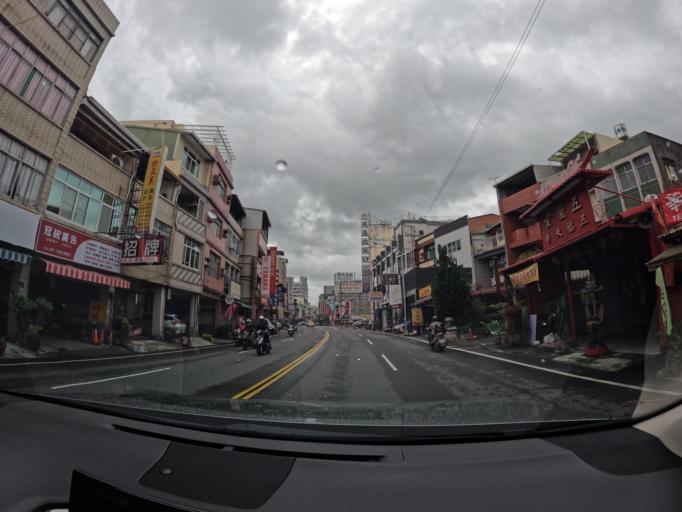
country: TW
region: Taiwan
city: Fengshan
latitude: 22.6267
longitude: 120.3528
